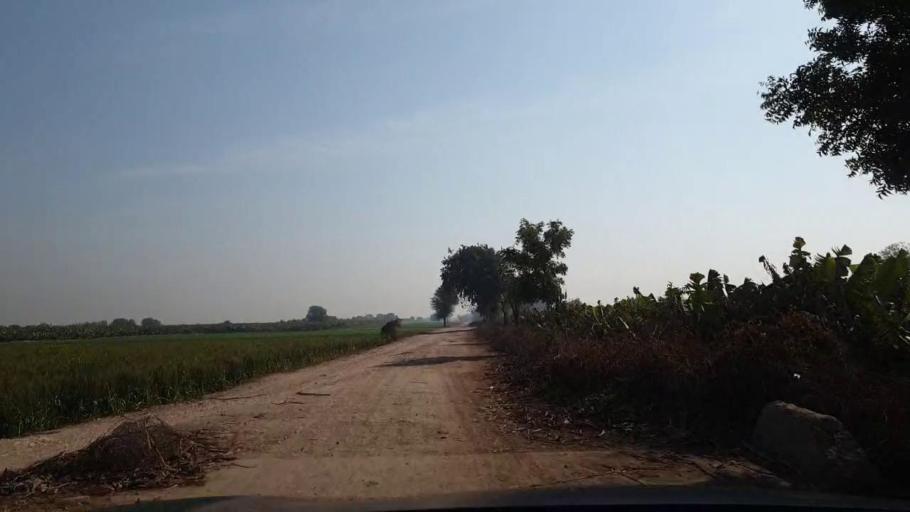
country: PK
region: Sindh
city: Tando Allahyar
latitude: 25.5935
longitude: 68.7371
